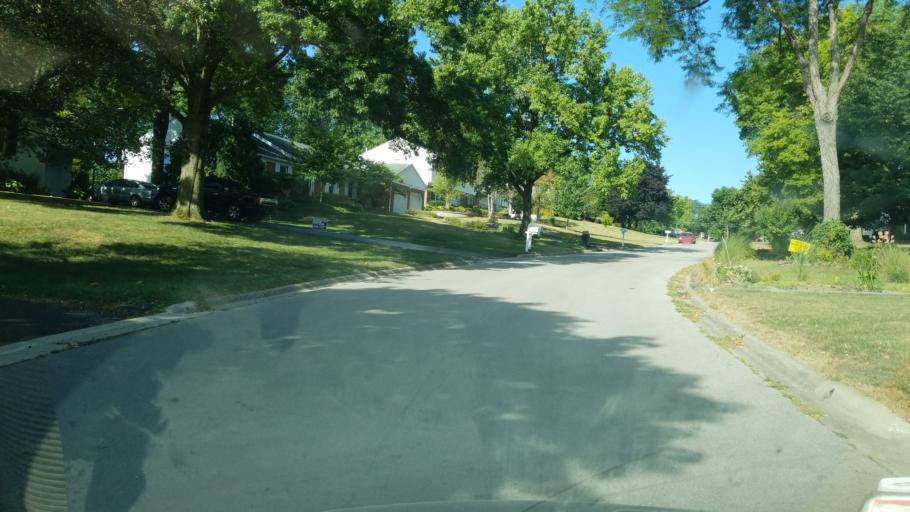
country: US
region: Ohio
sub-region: Franklin County
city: Worthington
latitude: 40.1258
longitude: -83.0388
